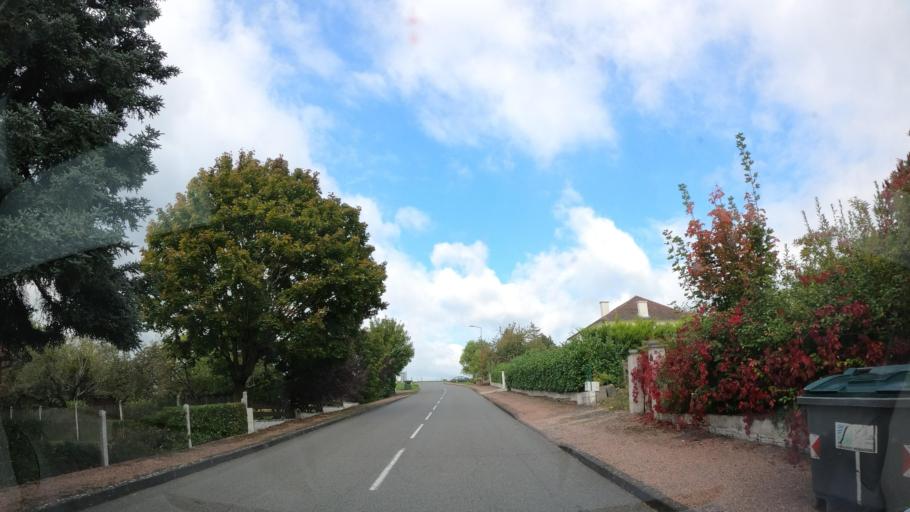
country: FR
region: Auvergne
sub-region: Departement de l'Allier
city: Lapalisse
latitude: 46.3303
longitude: 3.5944
